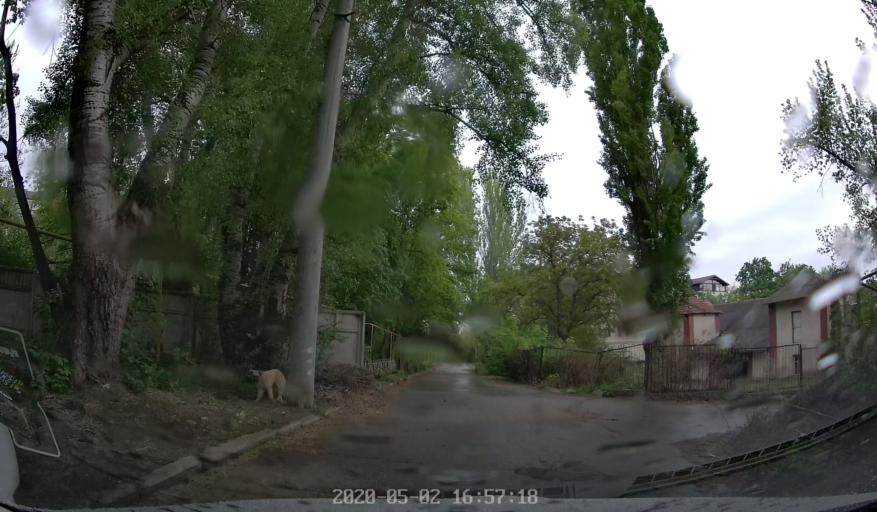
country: MD
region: Chisinau
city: Chisinau
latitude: 46.9744
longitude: 28.8330
